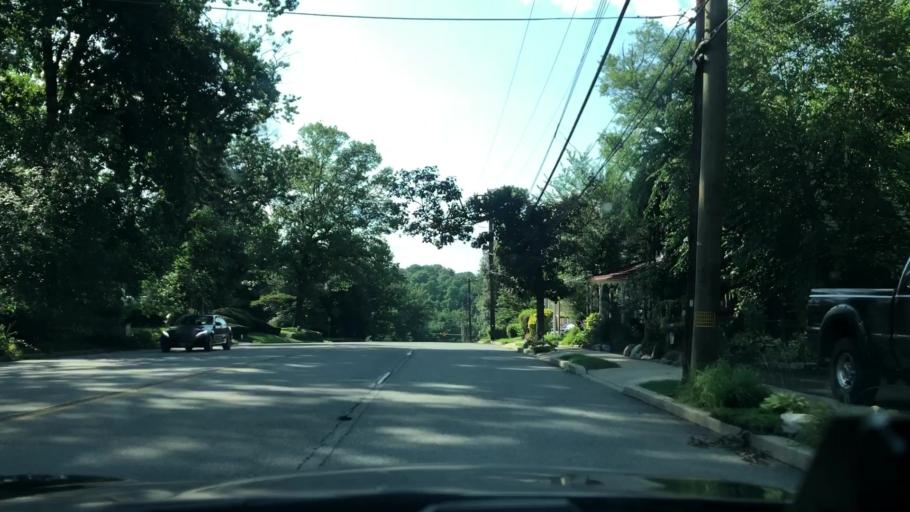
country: US
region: Pennsylvania
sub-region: Montgomery County
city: Wyndmoor
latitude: 40.0893
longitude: -75.1843
